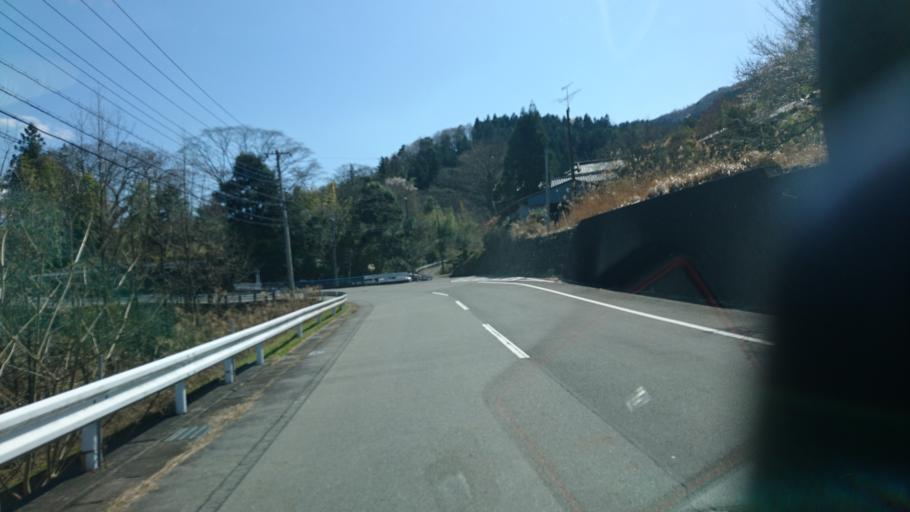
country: JP
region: Shizuoka
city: Fujinomiya
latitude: 35.3431
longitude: 138.4386
